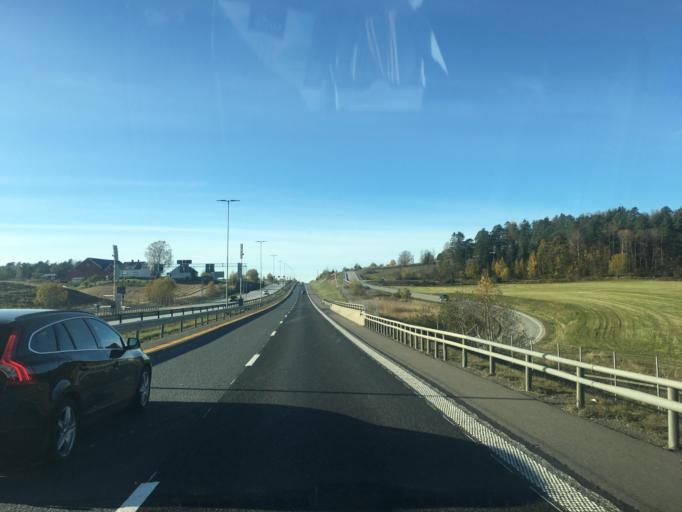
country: NO
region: Ostfold
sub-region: Fredrikstad
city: Fredrikstad
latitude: 59.3165
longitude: 10.9915
